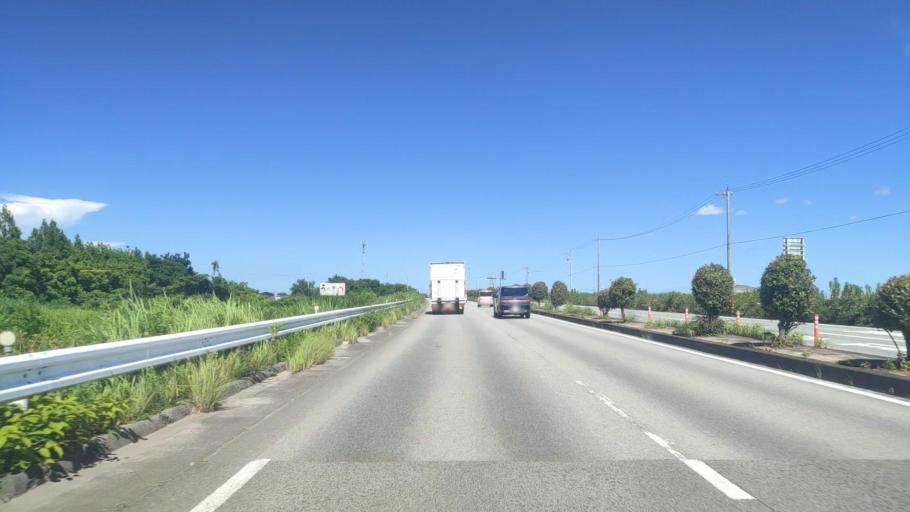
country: JP
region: Mie
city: Hisai-motomachi
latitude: 34.5836
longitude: 136.5686
